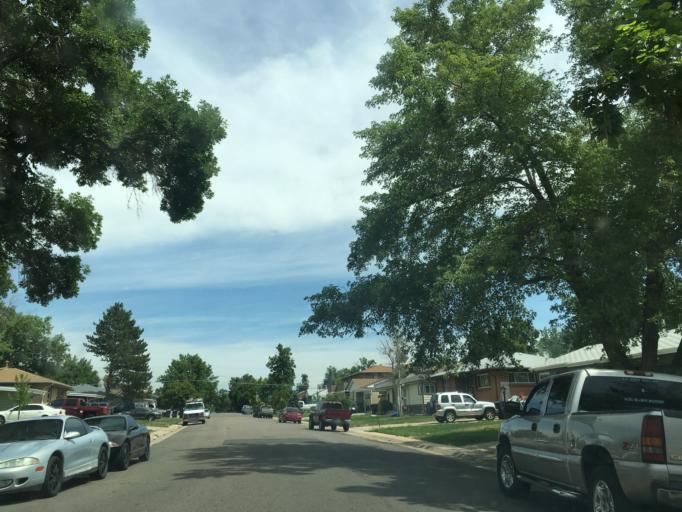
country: US
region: Colorado
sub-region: Jefferson County
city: Lakewood
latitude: 39.6884
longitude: -105.0411
